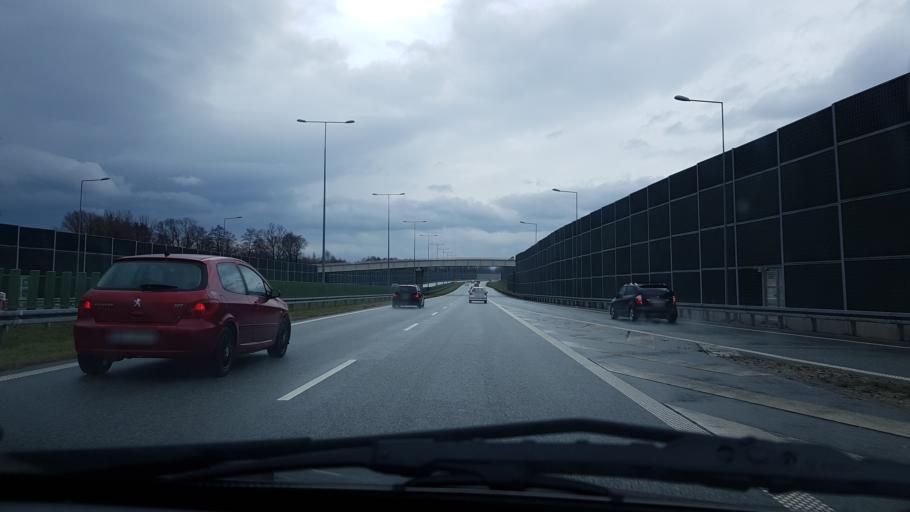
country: PL
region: Silesian Voivodeship
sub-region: Powiat bielski
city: Wilkowice
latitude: 49.7615
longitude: 19.0838
